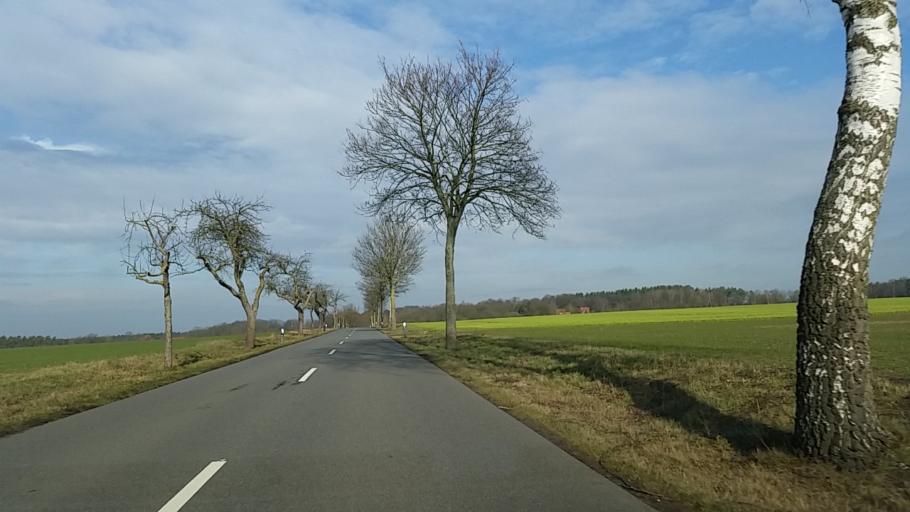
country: DE
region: Lower Saxony
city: Altenmedingen
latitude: 53.1620
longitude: 10.6191
